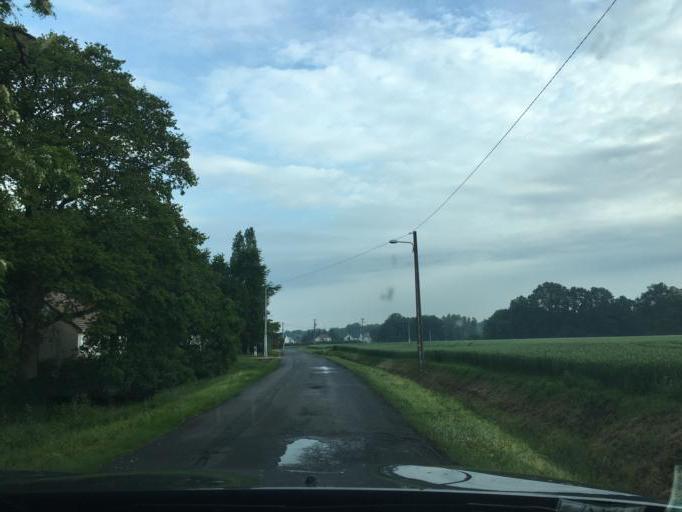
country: FR
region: Centre
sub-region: Departement du Loiret
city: Saint-Denis-en-Val
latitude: 47.8859
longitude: 1.9506
